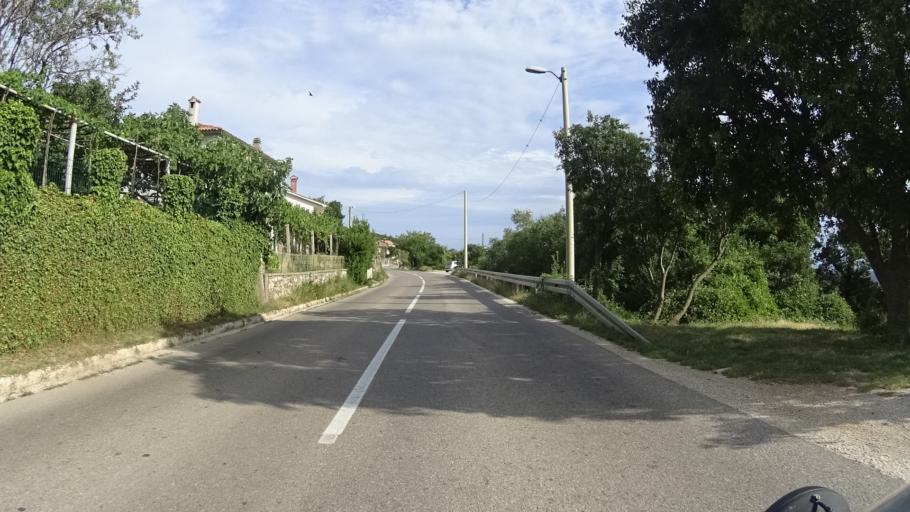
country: HR
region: Istarska
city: Rasa
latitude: 45.0139
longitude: 14.0938
